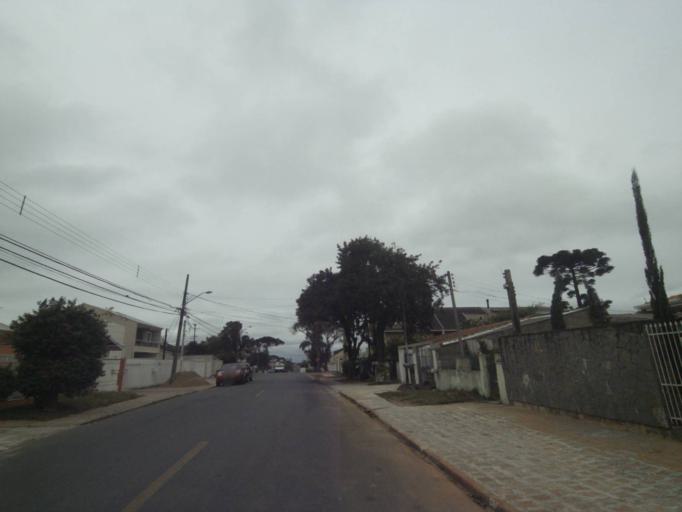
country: BR
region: Parana
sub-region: Sao Jose Dos Pinhais
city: Sao Jose dos Pinhais
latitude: -25.4824
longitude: -49.2315
